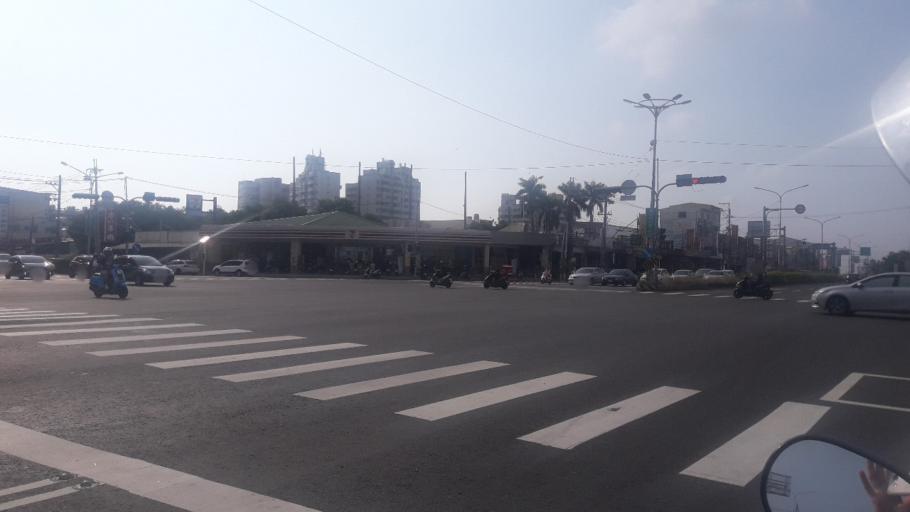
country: TW
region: Taiwan
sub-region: Tainan
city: Tainan
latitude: 22.8805
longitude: 120.2503
